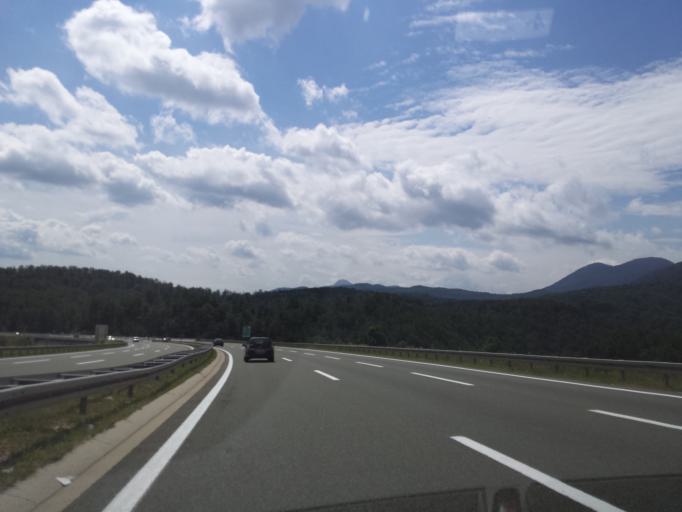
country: HR
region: Primorsko-Goranska
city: Vrbovsko
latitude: 45.3609
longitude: 15.0619
